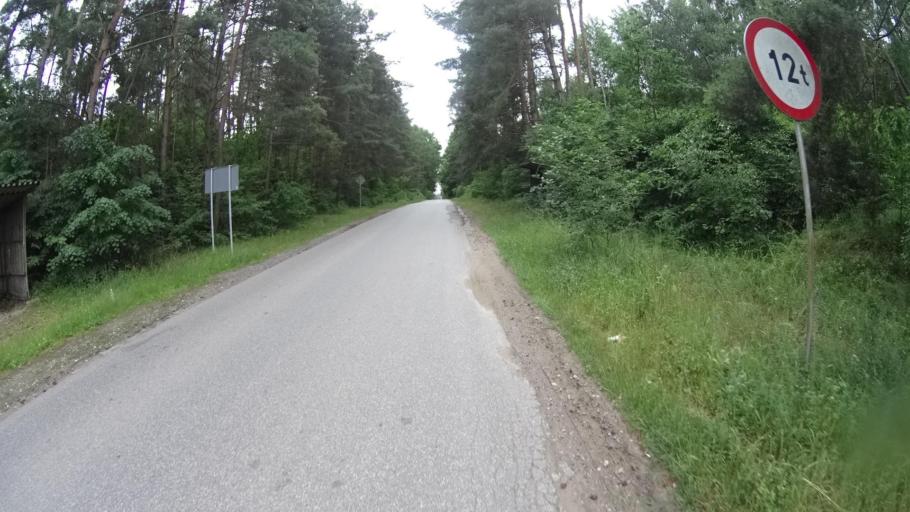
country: PL
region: Masovian Voivodeship
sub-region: Powiat grojecki
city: Belsk Duzy
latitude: 51.7997
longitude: 20.8594
